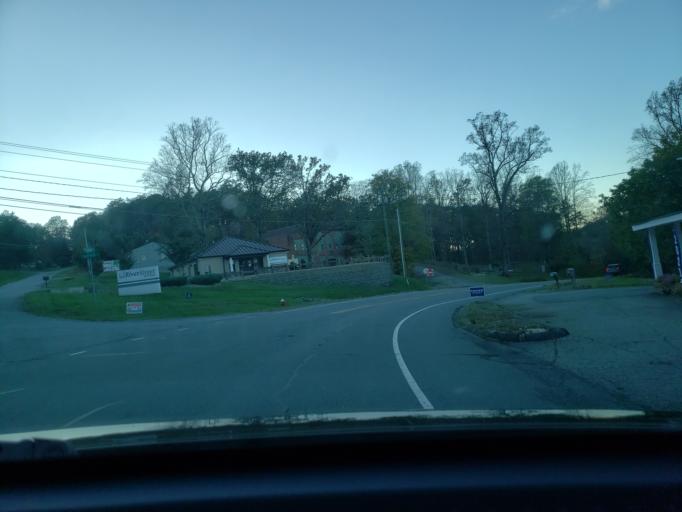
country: US
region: North Carolina
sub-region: Stokes County
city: Danbury
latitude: 36.4086
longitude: -80.2100
